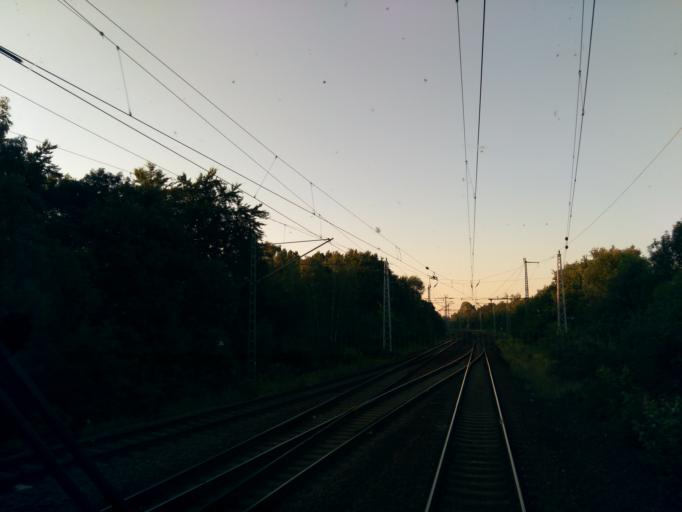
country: DE
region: Berlin
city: Adlershof
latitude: 52.4636
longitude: 13.5514
